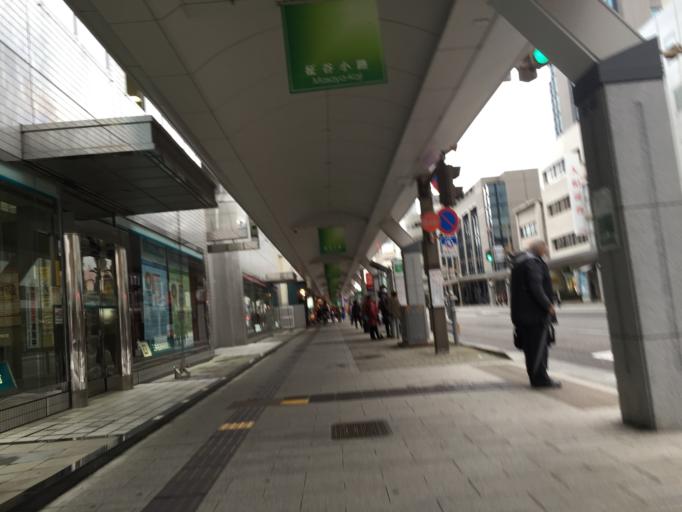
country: JP
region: Niigata
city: Niigata-shi
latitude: 37.9214
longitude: 139.0479
